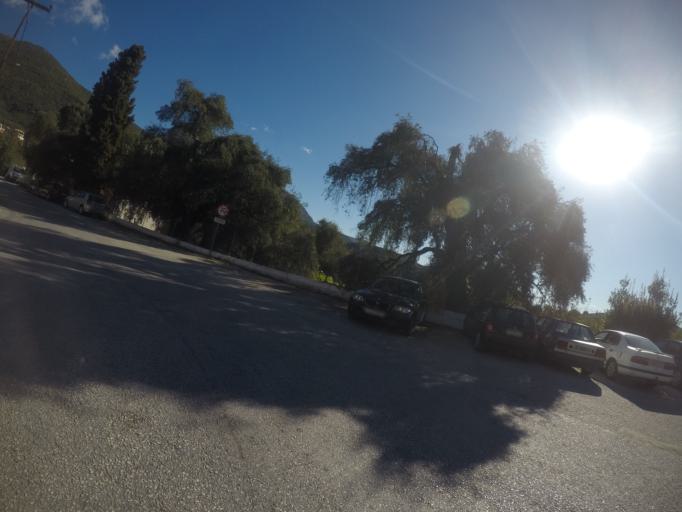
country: GR
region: Epirus
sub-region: Nomos Prevezis
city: Parga
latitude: 39.2866
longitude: 20.3960
